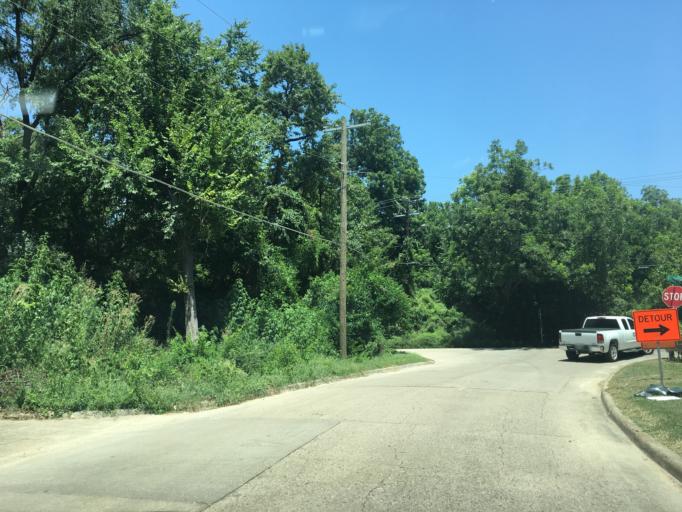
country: US
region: Texas
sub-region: Dallas County
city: Highland Park
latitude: 32.8377
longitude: -96.7319
